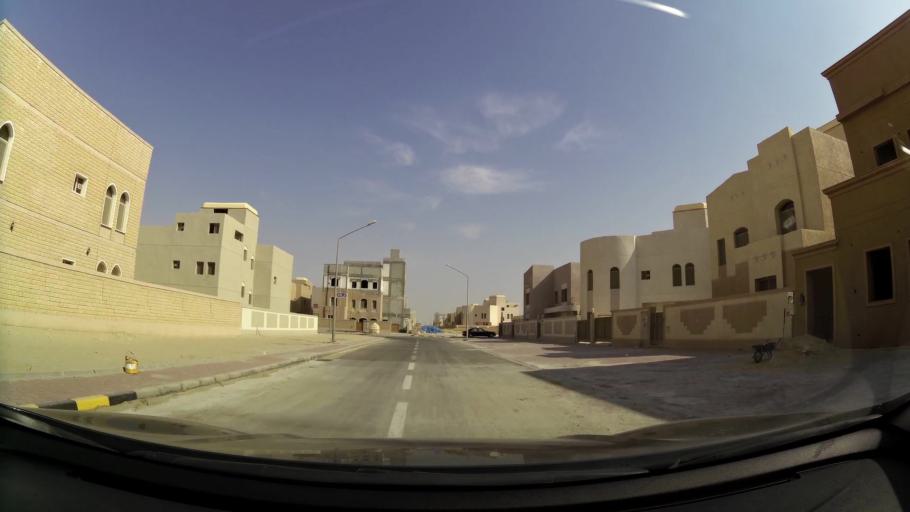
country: KW
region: Al Ahmadi
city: Al Wafrah
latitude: 28.7947
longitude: 48.0771
